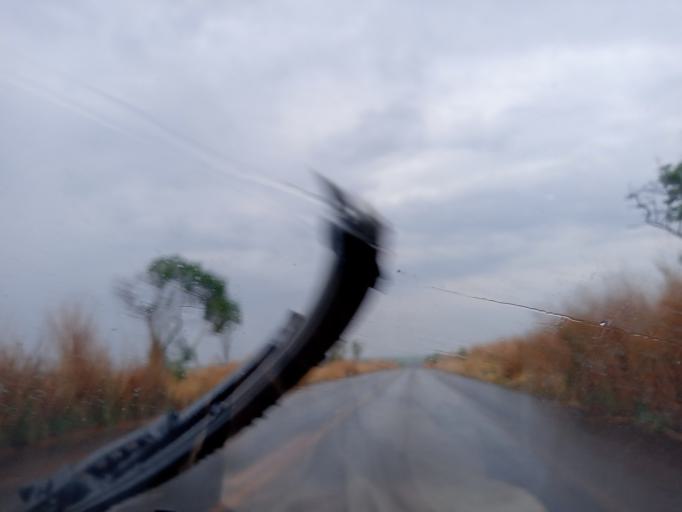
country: BR
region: Minas Gerais
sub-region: Ituiutaba
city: Ituiutaba
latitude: -19.1046
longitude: -49.5159
